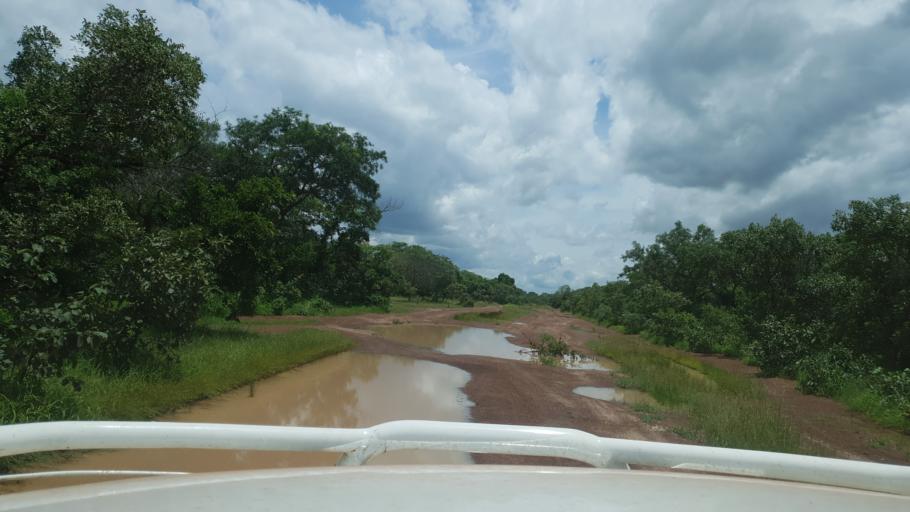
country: ML
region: Koulikoro
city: Banamba
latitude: 13.1985
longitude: -7.3283
